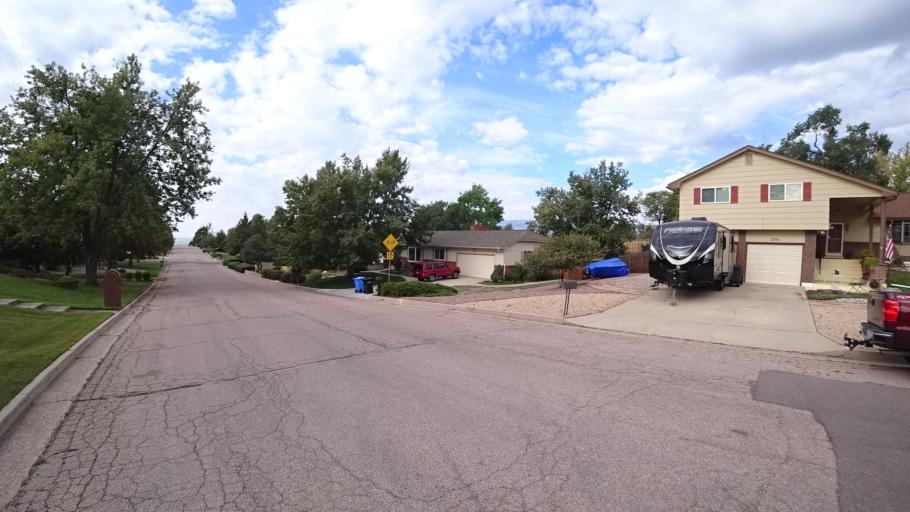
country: US
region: Colorado
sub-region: El Paso County
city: Cimarron Hills
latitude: 38.8668
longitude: -104.7457
